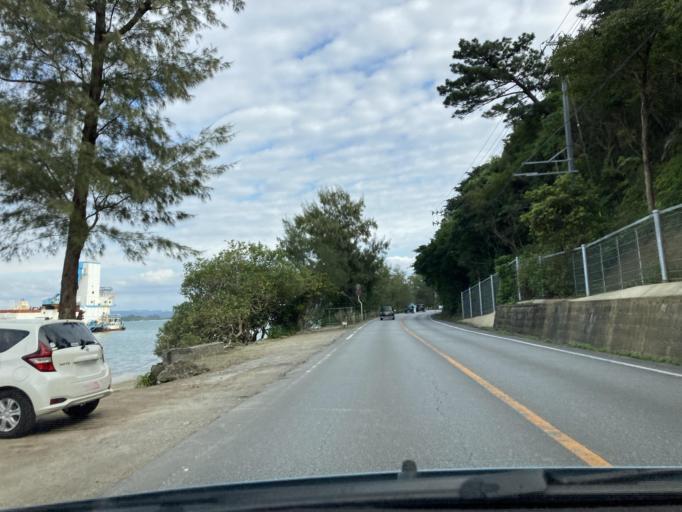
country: JP
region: Okinawa
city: Nago
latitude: 26.6455
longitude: 127.9933
